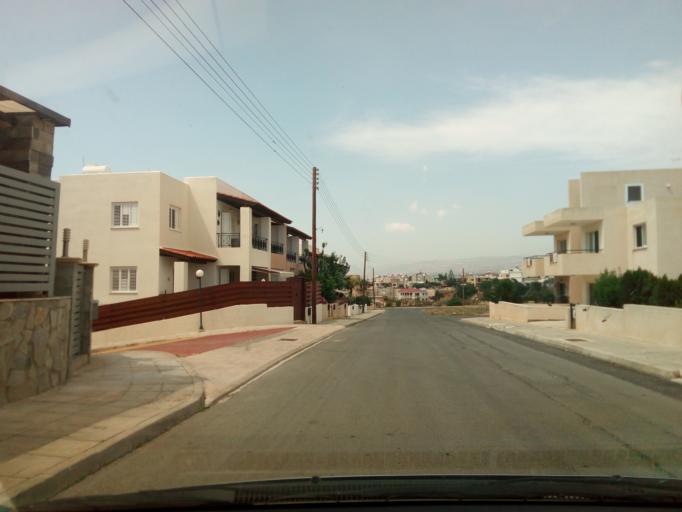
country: CY
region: Pafos
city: Chlorakas
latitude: 34.7915
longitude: 32.4102
